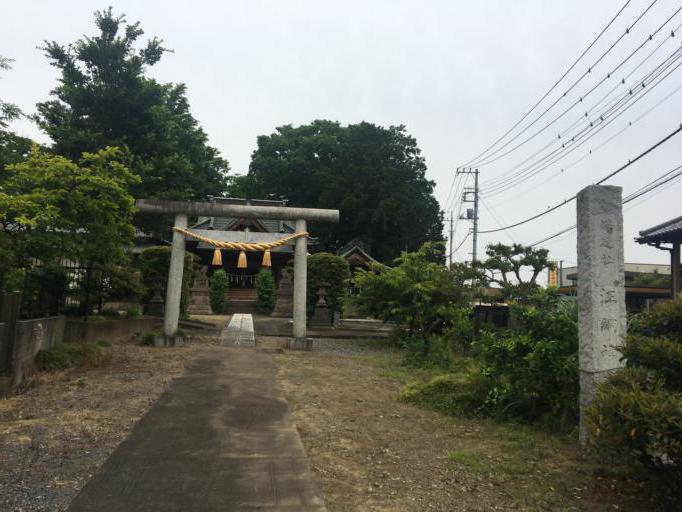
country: JP
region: Saitama
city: Fukiage-fujimi
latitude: 36.0231
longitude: 139.4533
